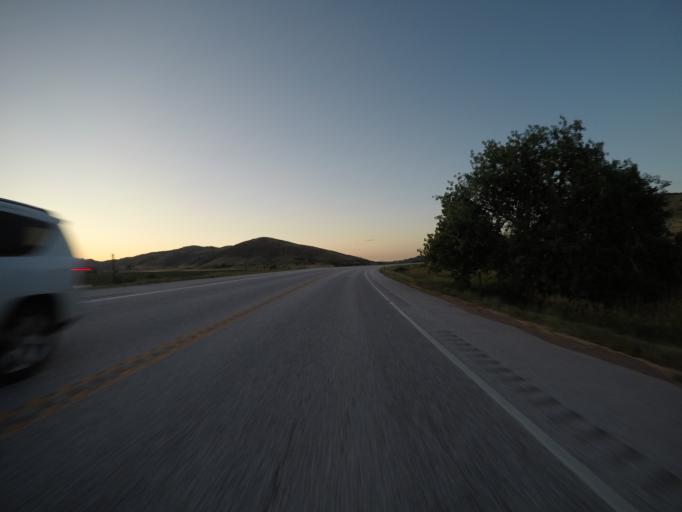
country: US
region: Colorado
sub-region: Larimer County
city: Laporte
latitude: 40.6695
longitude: -105.1910
